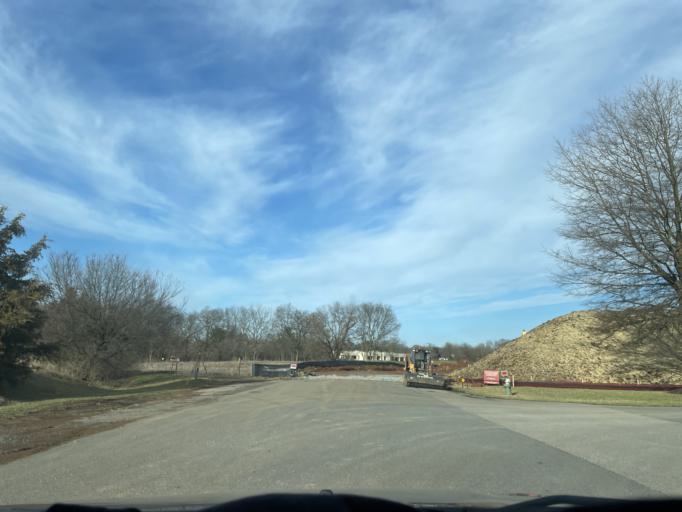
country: US
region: Maryland
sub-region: Washington County
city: Halfway
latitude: 39.6462
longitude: -77.7610
